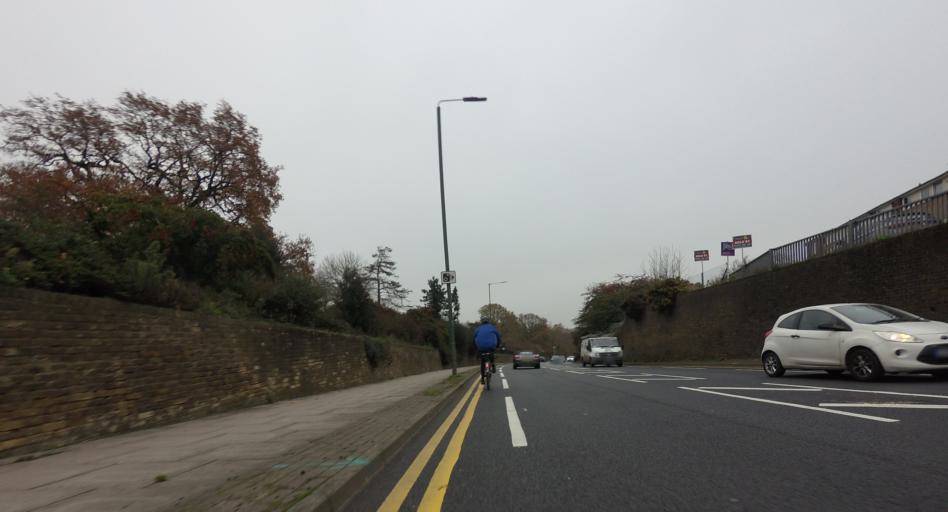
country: GB
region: England
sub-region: Greater London
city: Bexley
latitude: 51.4510
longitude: 0.1541
